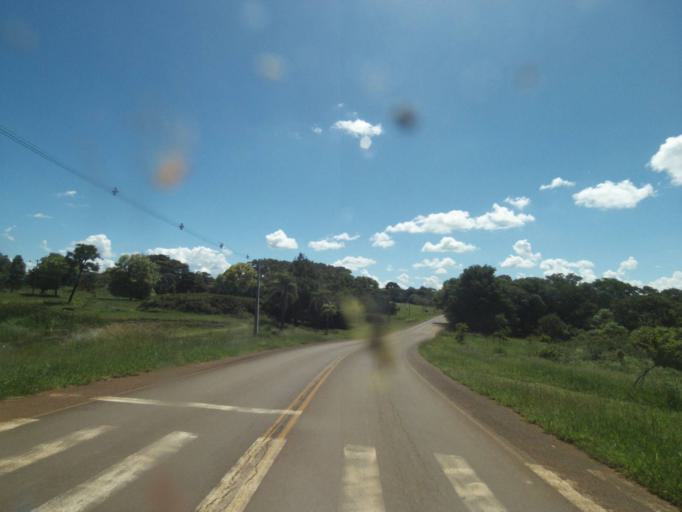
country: BR
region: Parana
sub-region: Pinhao
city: Pinhao
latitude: -25.7917
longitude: -52.0855
